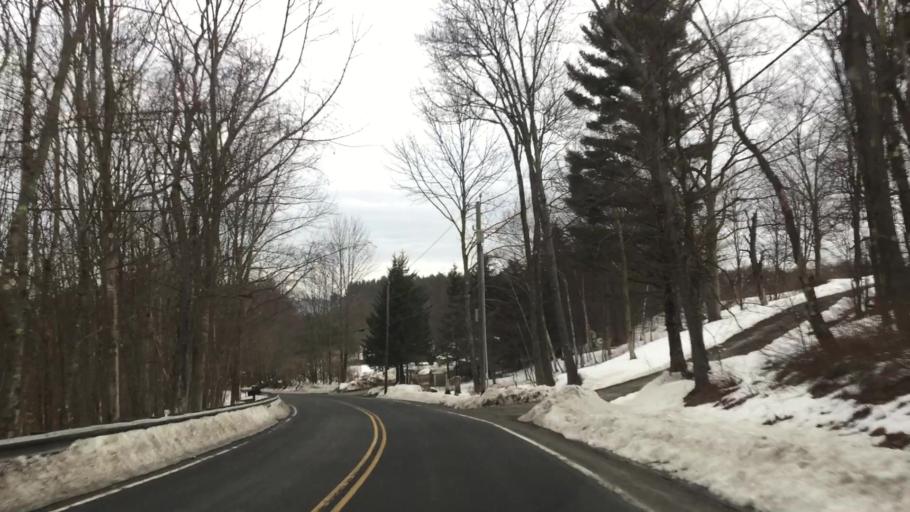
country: US
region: Massachusetts
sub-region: Berkshire County
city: Hinsdale
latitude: 42.4178
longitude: -73.0703
